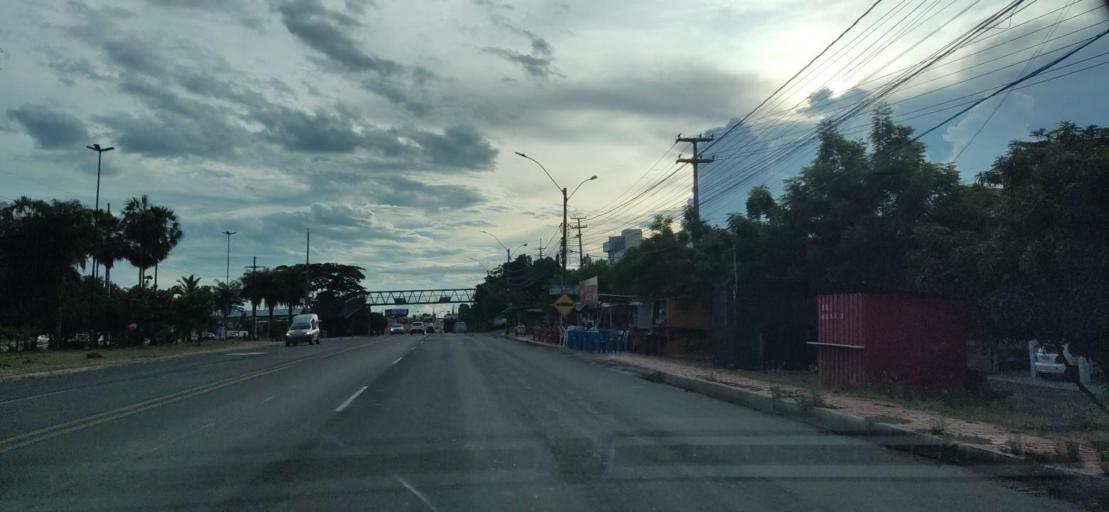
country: BR
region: Piaui
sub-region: Teresina
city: Teresina
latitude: -5.1176
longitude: -42.7844
